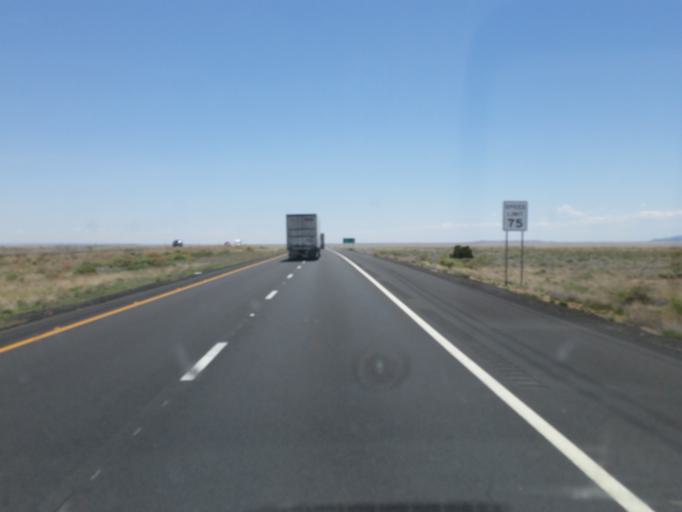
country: US
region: Arizona
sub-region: Coconino County
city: LeChee
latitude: 35.1251
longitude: -111.1735
